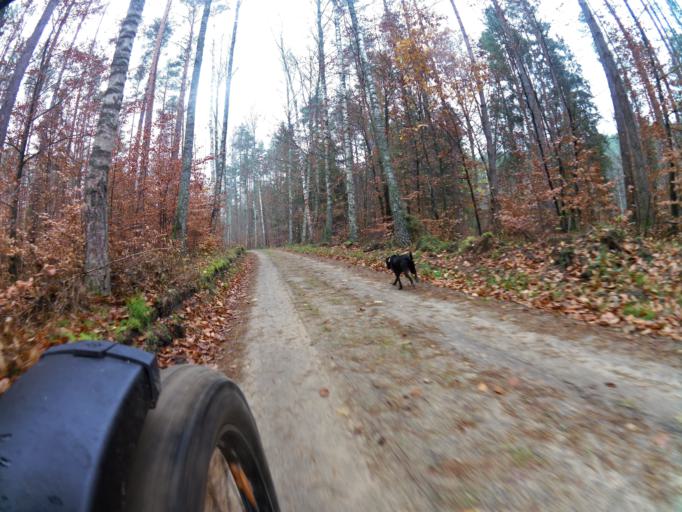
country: PL
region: Pomeranian Voivodeship
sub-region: Powiat wejherowski
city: Orle
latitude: 54.6932
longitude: 18.1564
